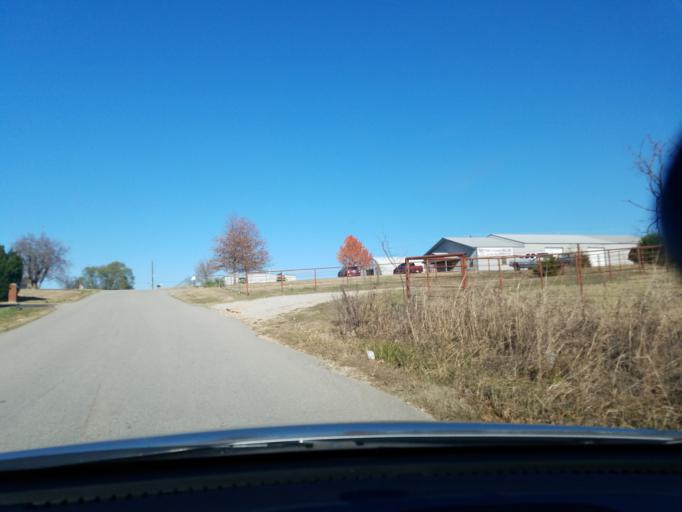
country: US
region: Arkansas
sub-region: Carroll County
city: Berryville
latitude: 36.3845
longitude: -93.6035
